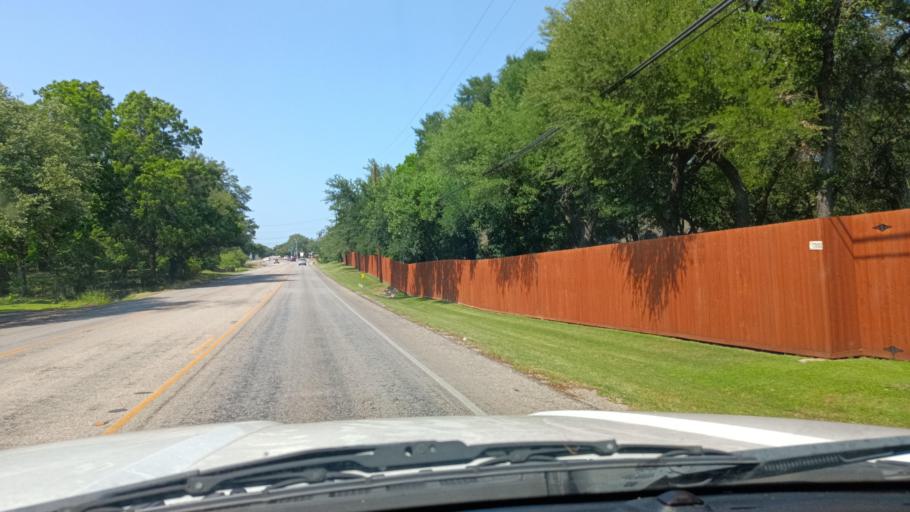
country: US
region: Texas
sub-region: Bell County
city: Morgans Point Resort
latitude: 31.1252
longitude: -97.4699
